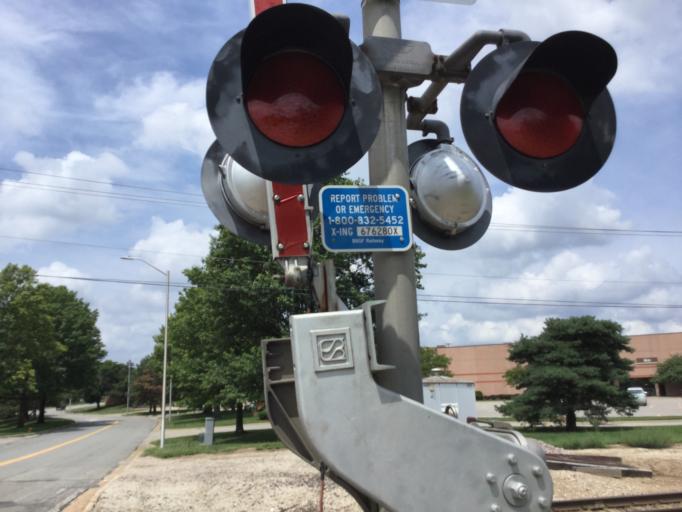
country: US
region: Kansas
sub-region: Johnson County
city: Lenexa
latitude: 38.9840
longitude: -94.7124
